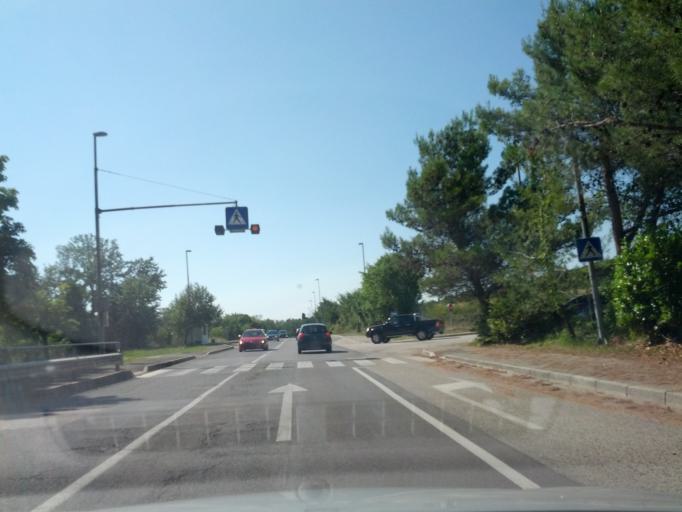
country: SI
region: Koper-Capodistria
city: Hrvatini
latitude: 45.5713
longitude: 13.7488
